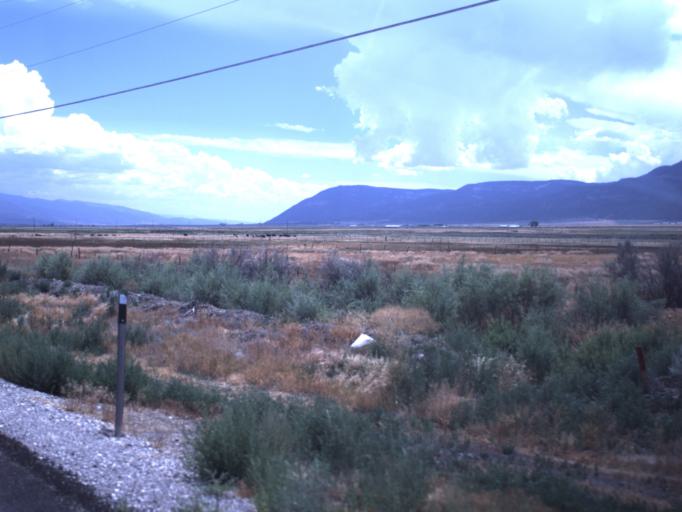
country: US
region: Utah
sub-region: Sanpete County
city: Moroni
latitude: 39.5728
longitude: -111.6082
